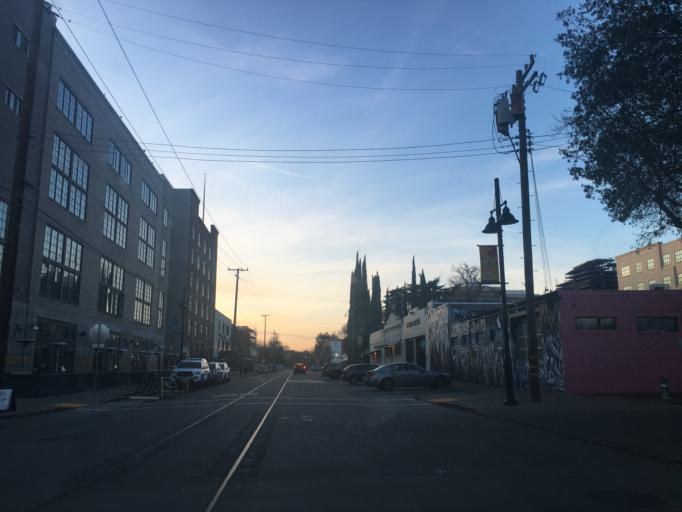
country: US
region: California
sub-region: Sacramento County
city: Sacramento
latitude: 38.5708
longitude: -121.4945
